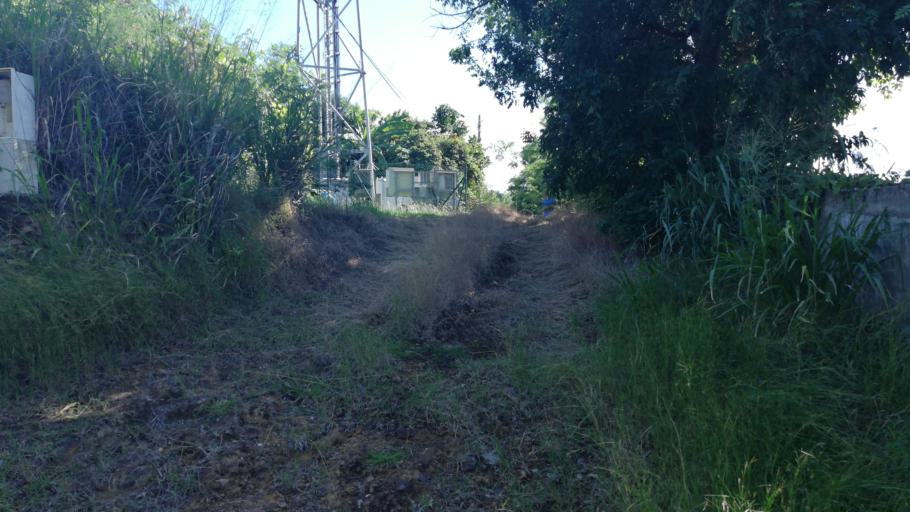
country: GP
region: Guadeloupe
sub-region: Guadeloupe
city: Vieux-Habitants
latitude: 16.0543
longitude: -61.7579
